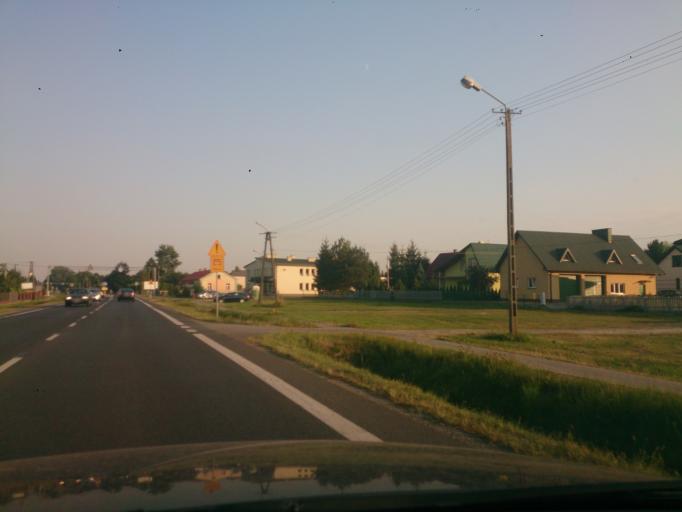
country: PL
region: Subcarpathian Voivodeship
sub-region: Powiat kolbuszowski
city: Kolbuszowa
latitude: 50.2281
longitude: 21.7920
